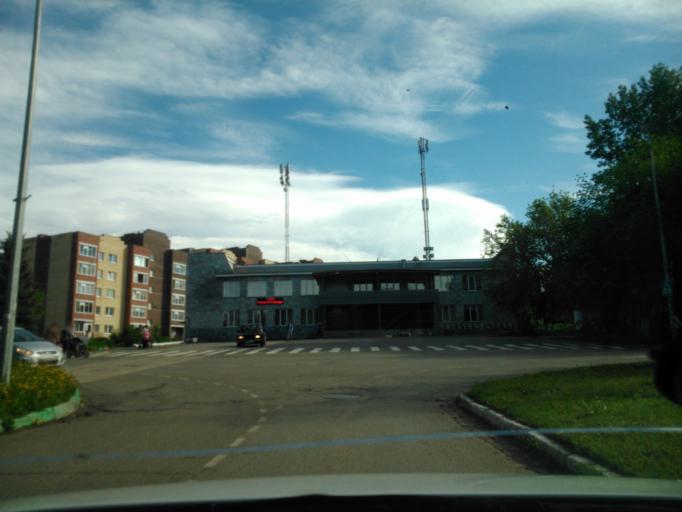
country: RU
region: Perm
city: Lobanovo
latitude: 57.8625
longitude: 56.2883
